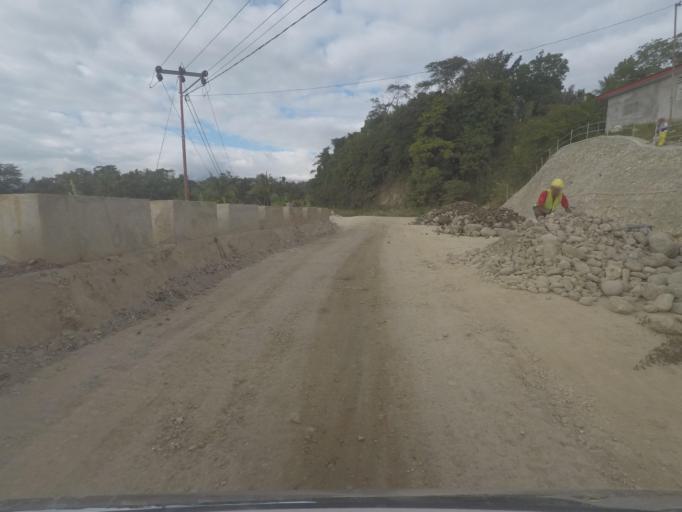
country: TL
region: Baucau
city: Venilale
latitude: -8.6075
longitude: 126.3826
